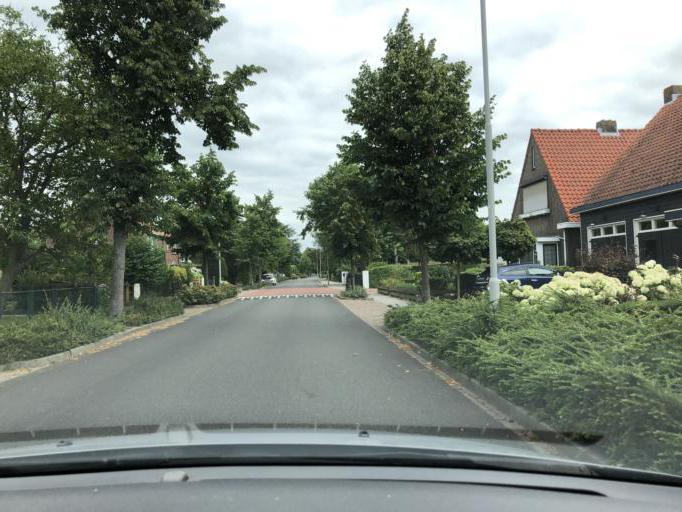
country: NL
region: Zeeland
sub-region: Gemeente Reimerswaal
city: Yerseke
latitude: 51.4193
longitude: 4.0687
